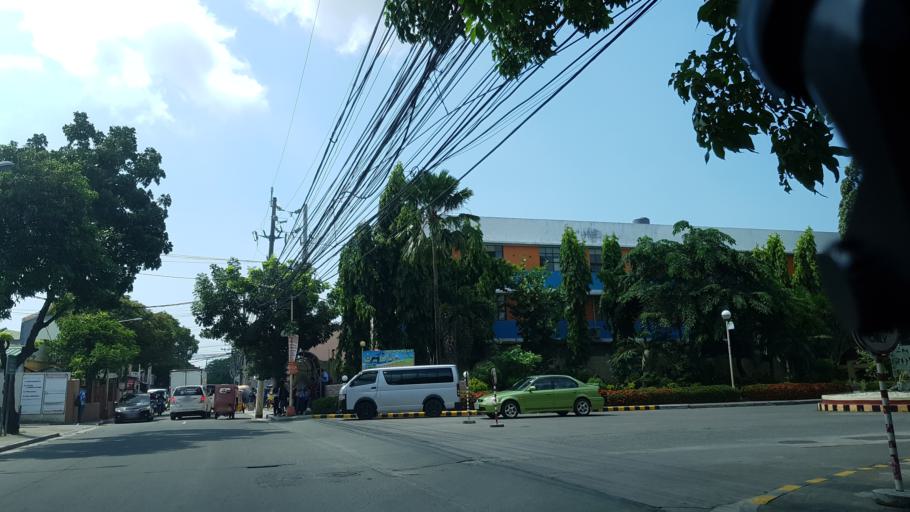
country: PH
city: Sambayanihan People's Village
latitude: 14.4638
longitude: 120.9876
